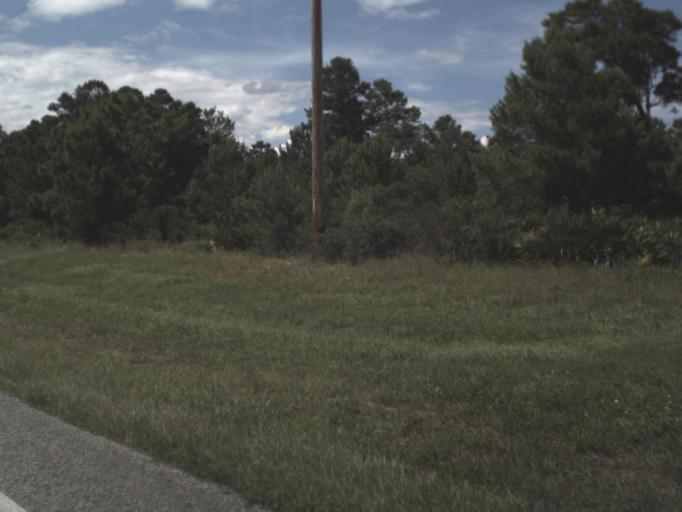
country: US
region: Florida
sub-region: Polk County
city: Babson Park
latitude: 27.8829
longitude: -81.4464
